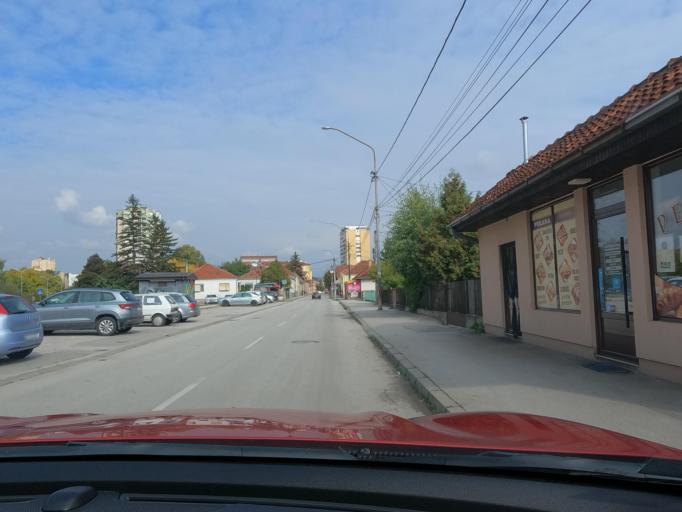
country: RS
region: Central Serbia
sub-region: Moravicki Okrug
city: Cacak
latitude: 43.8849
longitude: 20.3427
